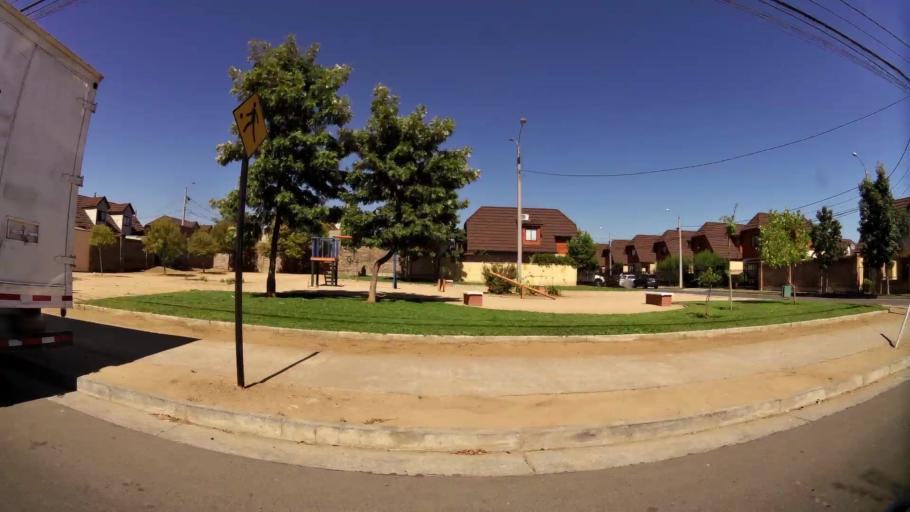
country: CL
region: Maule
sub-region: Provincia de Talca
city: Talca
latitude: -35.4295
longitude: -71.6169
